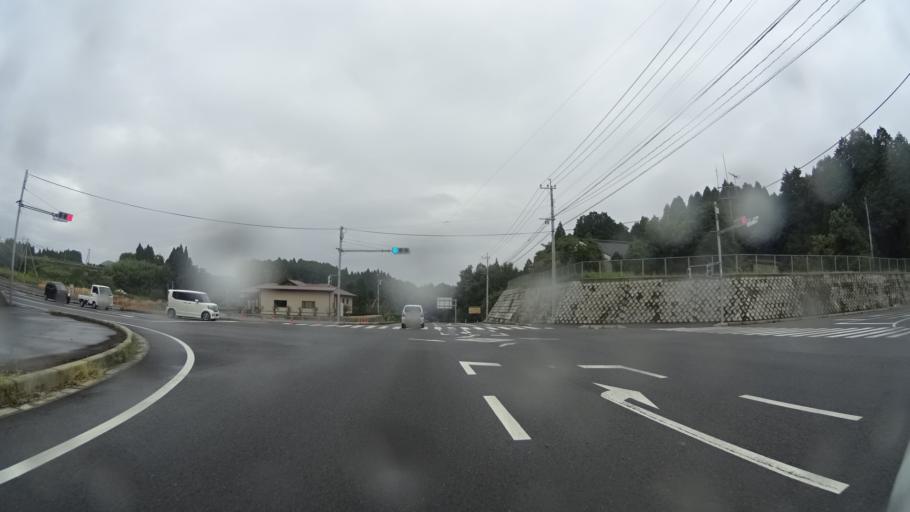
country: JP
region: Kagoshima
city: Kajiki
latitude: 31.8118
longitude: 130.6775
